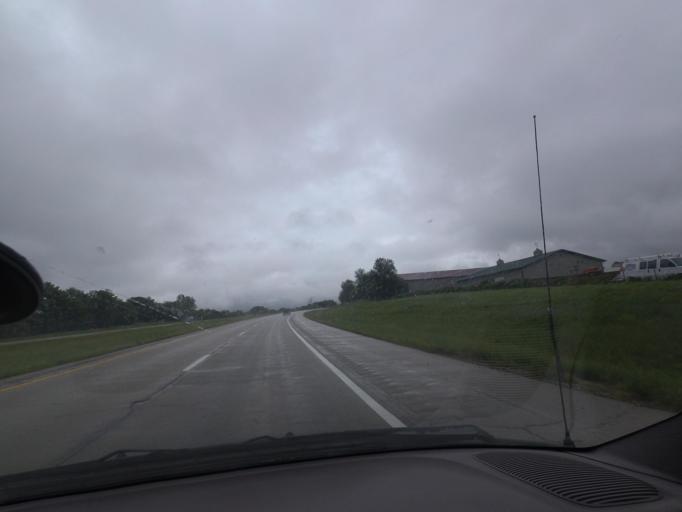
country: US
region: Illinois
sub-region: Champaign County
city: Champaign
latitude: 40.1197
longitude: -88.2924
